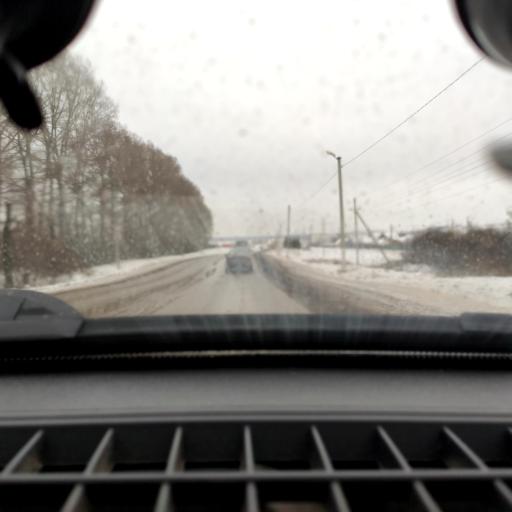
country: RU
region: Bashkortostan
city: Iglino
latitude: 54.8091
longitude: 56.4105
